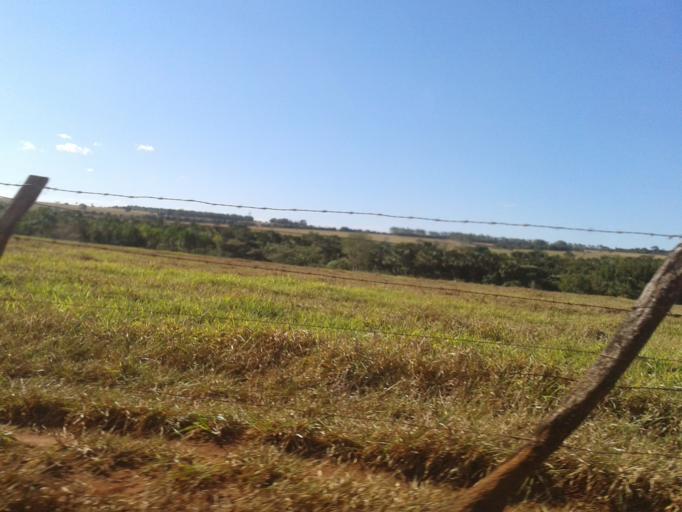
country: BR
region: Minas Gerais
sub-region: Centralina
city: Centralina
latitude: -18.7377
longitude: -49.1712
